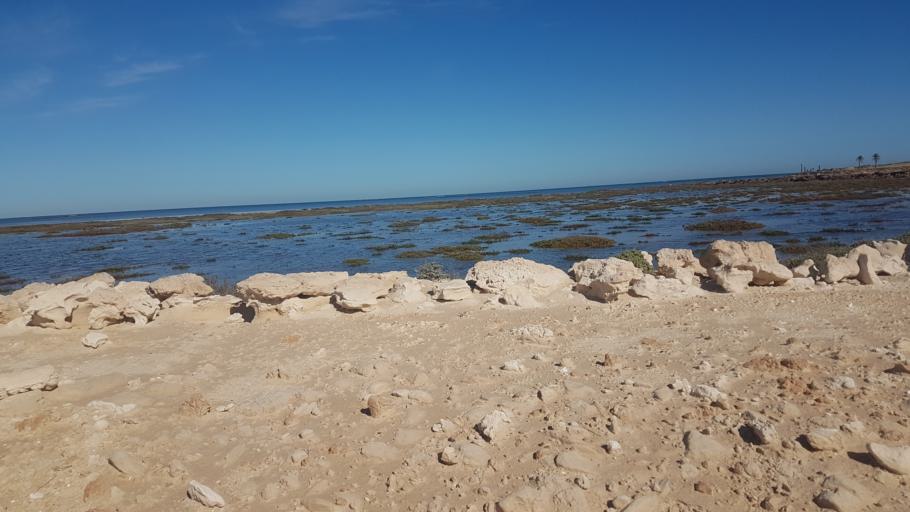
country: TN
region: Safaqis
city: Al Qarmadah
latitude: 34.6670
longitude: 11.0509
